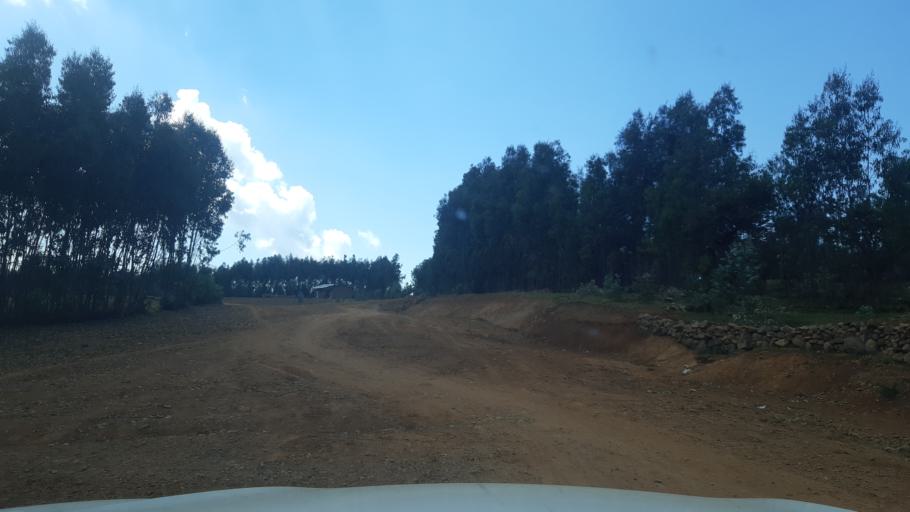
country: ET
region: Amhara
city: Dabat
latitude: 13.3625
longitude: 37.3843
